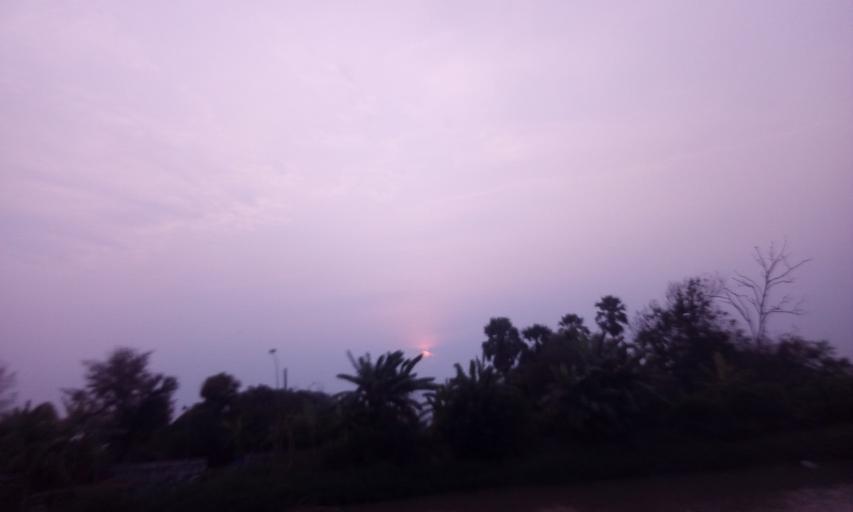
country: TH
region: Pathum Thani
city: Nong Suea
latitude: 14.0377
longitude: 100.8936
